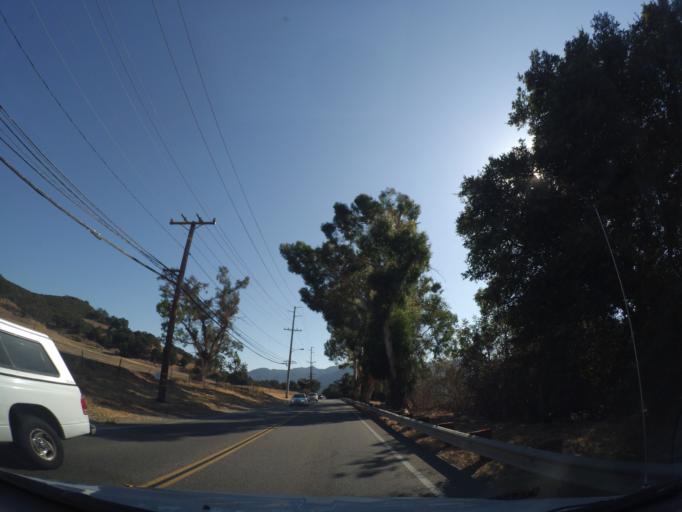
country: US
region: California
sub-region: Los Angeles County
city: Agoura
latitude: 34.1121
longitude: -118.7106
